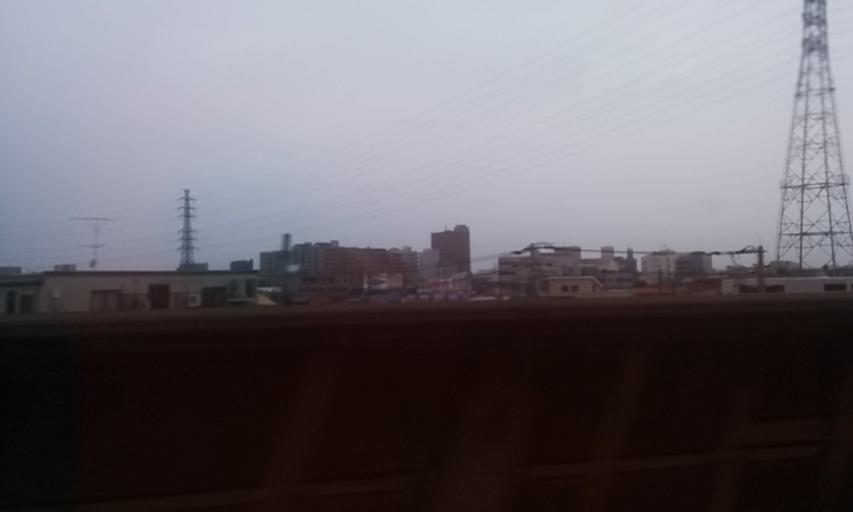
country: JP
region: Saitama
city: Ageoshimo
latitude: 35.9383
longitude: 139.6174
